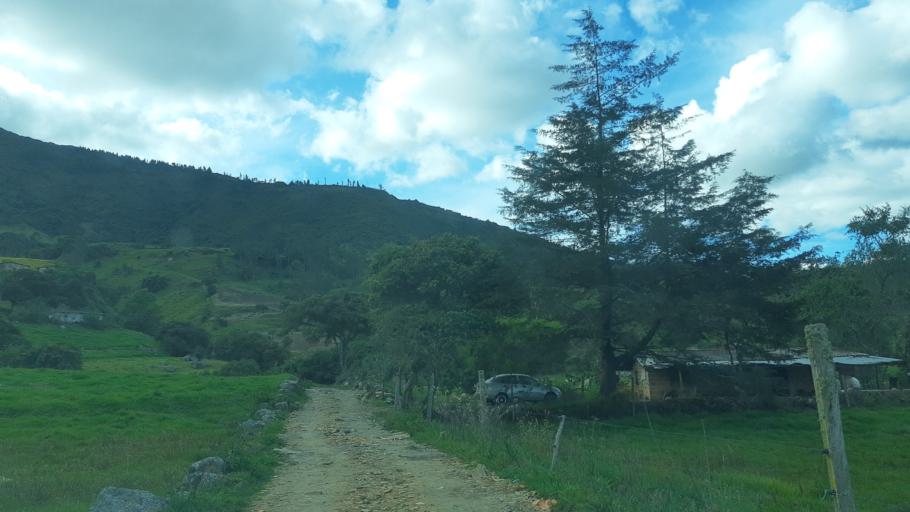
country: CO
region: Cundinamarca
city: Macheta
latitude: 5.0725
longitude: -73.6338
